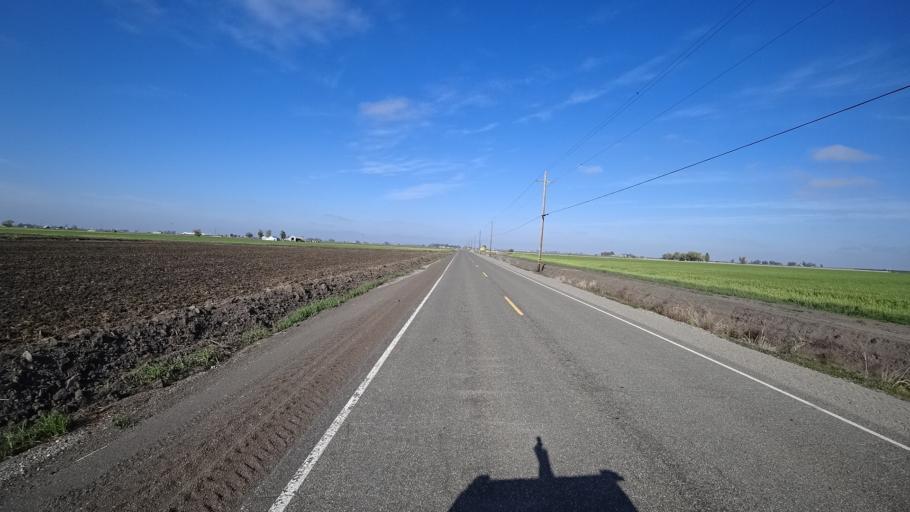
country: US
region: California
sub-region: Glenn County
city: Willows
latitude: 39.5827
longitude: -122.0713
